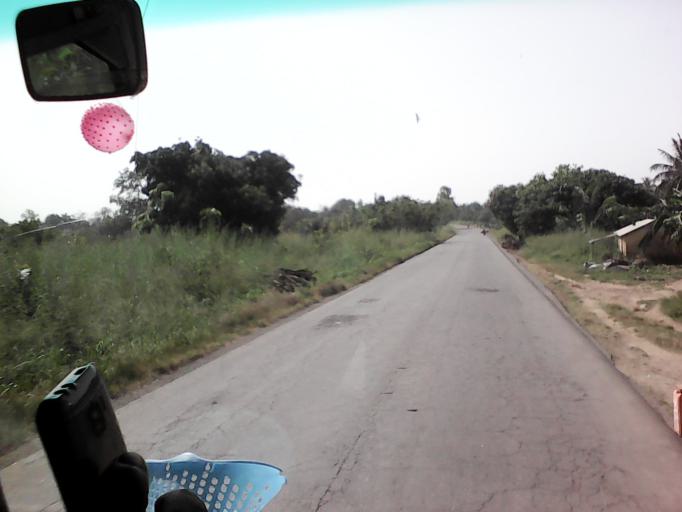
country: TG
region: Centrale
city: Sokode
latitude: 8.8464
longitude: 1.0717
